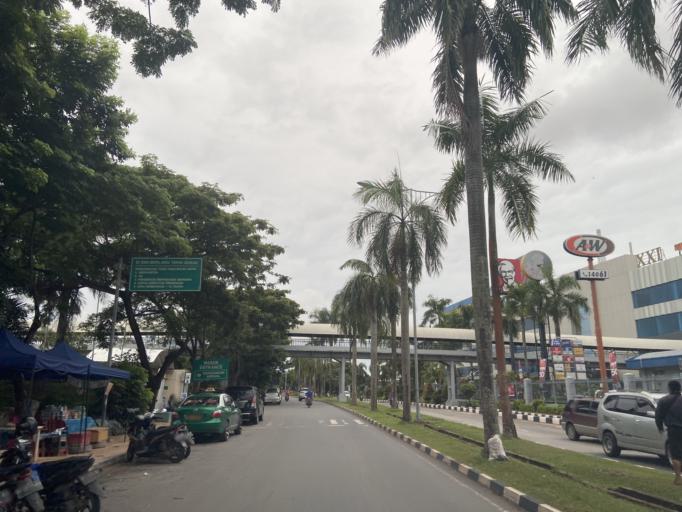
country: SG
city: Singapore
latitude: 1.1300
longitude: 104.0549
